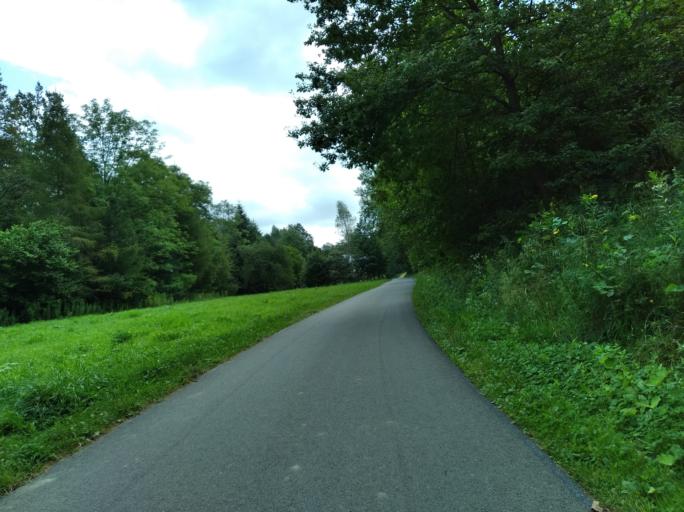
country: PL
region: Subcarpathian Voivodeship
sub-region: Powiat krosnienski
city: Wojaszowka
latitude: 49.7841
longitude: 21.7031
